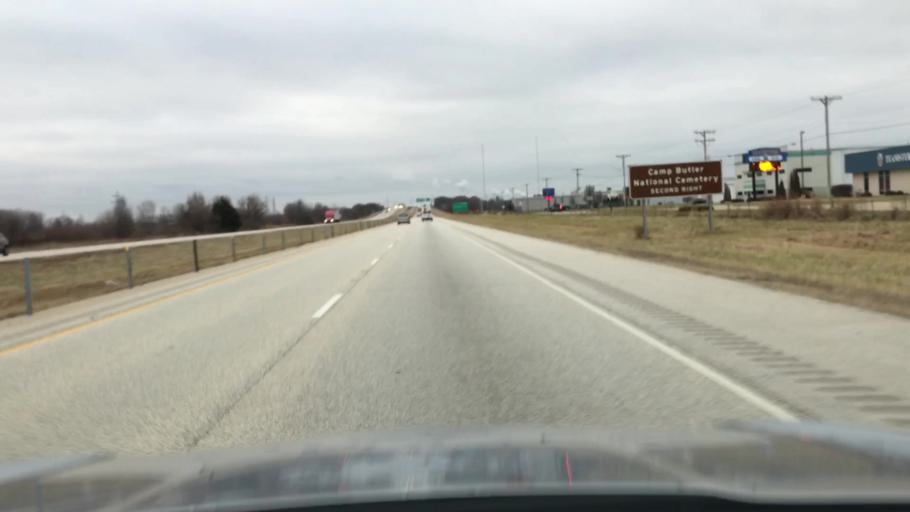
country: US
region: Illinois
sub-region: Sangamon County
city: Grandview
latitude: 39.8440
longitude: -89.5943
